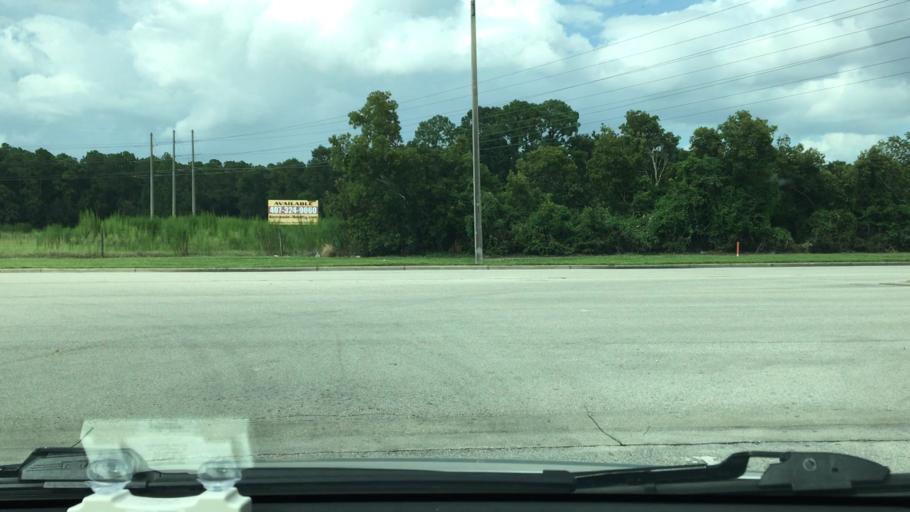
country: US
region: Florida
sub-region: Seminole County
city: Lake Mary
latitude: 28.8041
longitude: -81.3279
